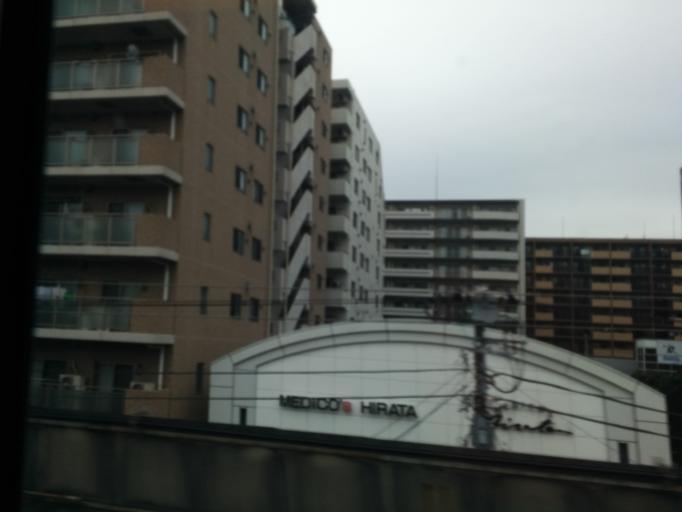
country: JP
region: Kanagawa
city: Yokohama
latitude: 35.5020
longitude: 139.6106
